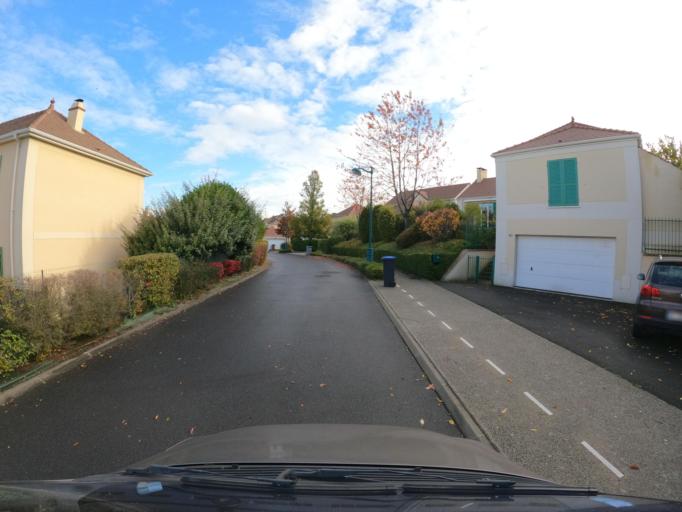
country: FR
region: Ile-de-France
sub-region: Departement de Seine-et-Marne
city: Magny-le-Hongre
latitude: 48.8691
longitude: 2.8217
